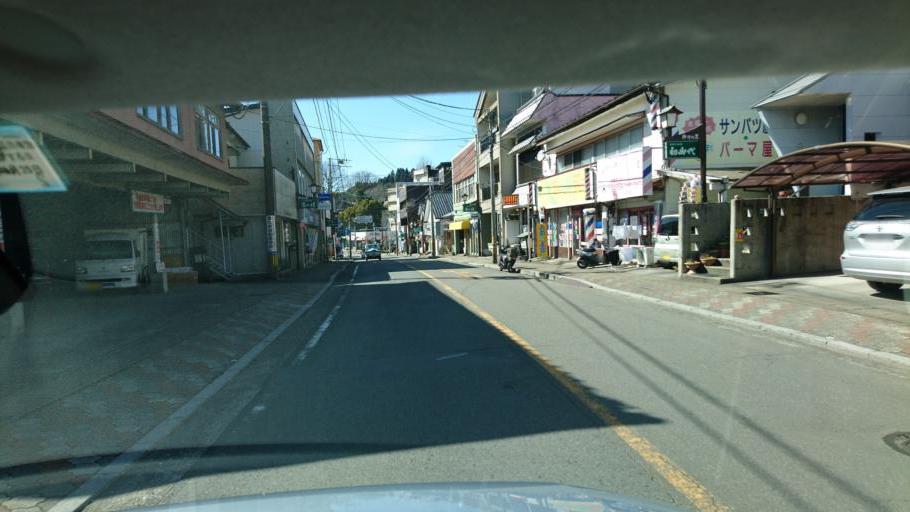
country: JP
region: Oita
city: Takedamachi
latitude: 32.7109
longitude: 131.3100
